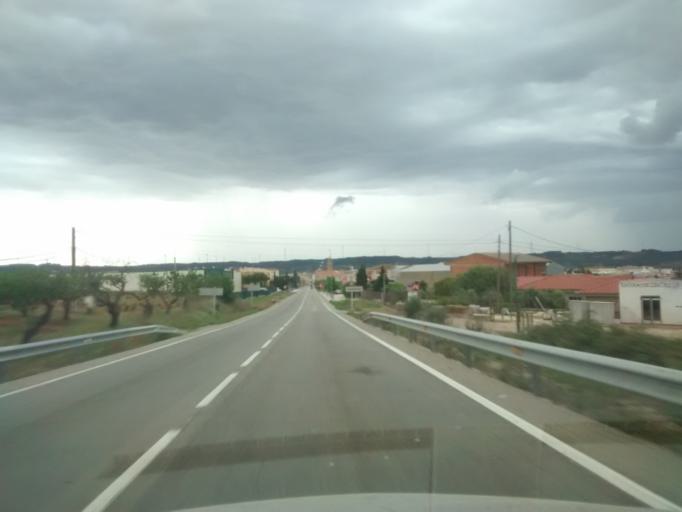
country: ES
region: Catalonia
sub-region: Provincia de Tarragona
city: Gandesa
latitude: 41.0482
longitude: 0.4480
